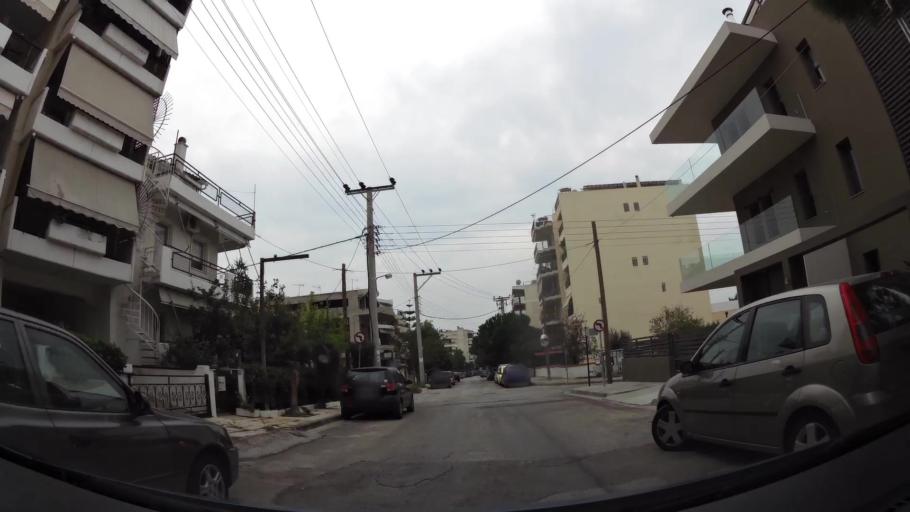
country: GR
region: Attica
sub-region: Nomarchia Athinas
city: Alimos
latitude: 37.9179
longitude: 23.7246
